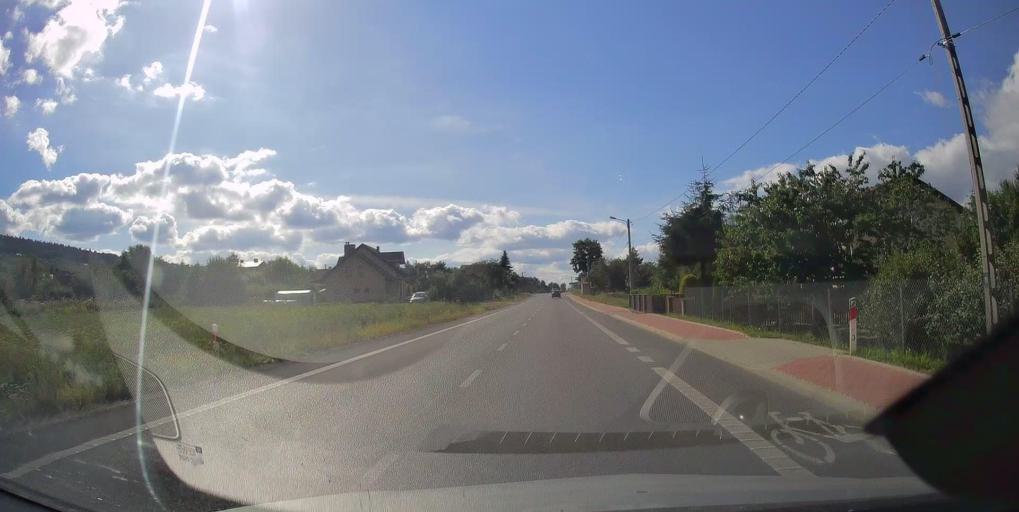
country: PL
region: Swietokrzyskie
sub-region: Powiat kielecki
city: Bodzentyn
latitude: 50.9357
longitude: 20.9599
